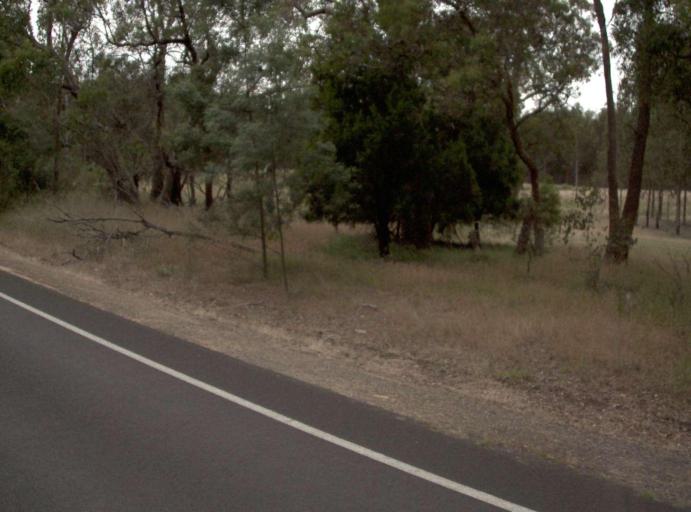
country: AU
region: Victoria
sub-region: Wellington
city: Sale
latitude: -38.4268
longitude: 146.9543
